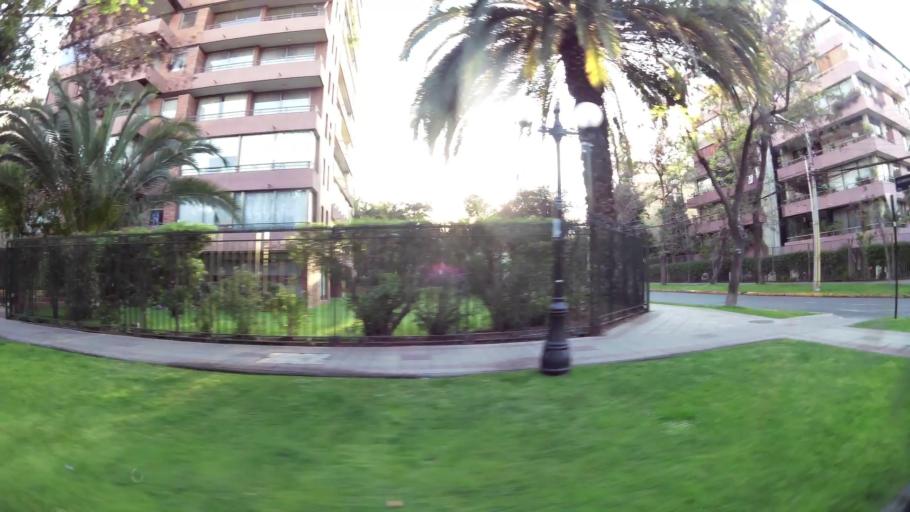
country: CL
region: Santiago Metropolitan
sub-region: Provincia de Santiago
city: Villa Presidente Frei, Nunoa, Santiago, Chile
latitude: -33.4276
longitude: -70.6012
